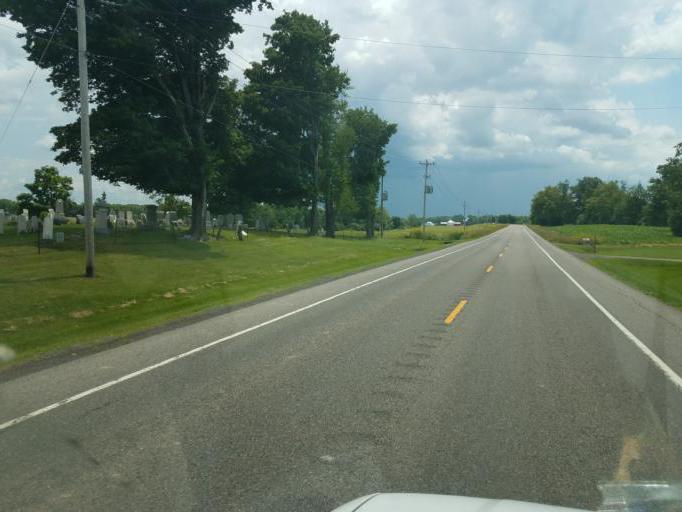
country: US
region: New York
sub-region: Seneca County
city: Waterloo
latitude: 42.9934
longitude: -76.8527
